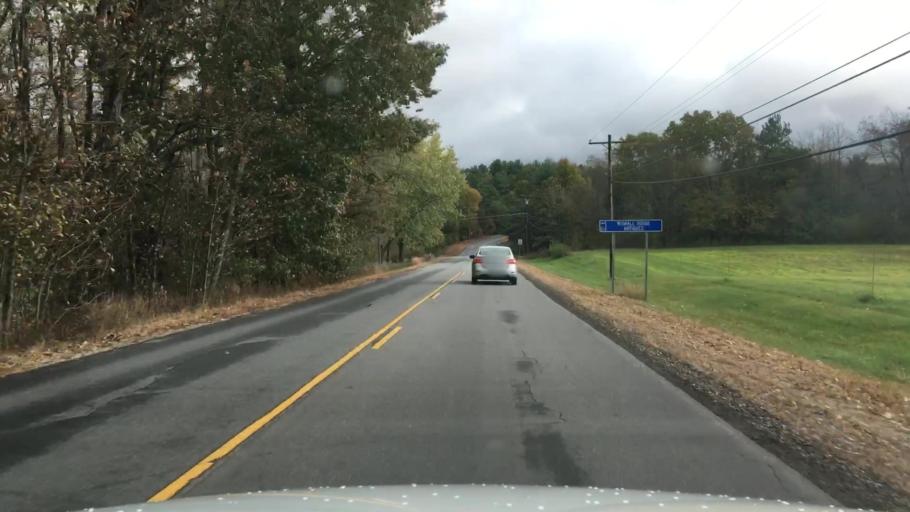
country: US
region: New Hampshire
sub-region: Strafford County
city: Lee
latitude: 43.0983
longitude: -70.9859
